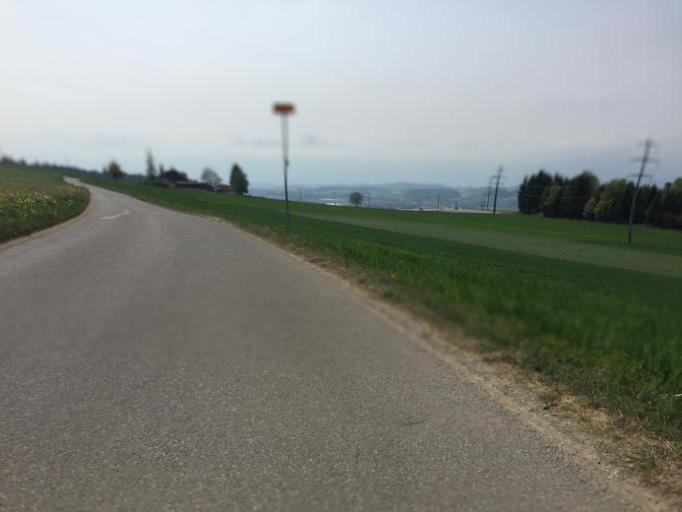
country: CH
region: Bern
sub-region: Bern-Mittelland District
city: Taegertschi
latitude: 46.8650
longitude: 7.5813
